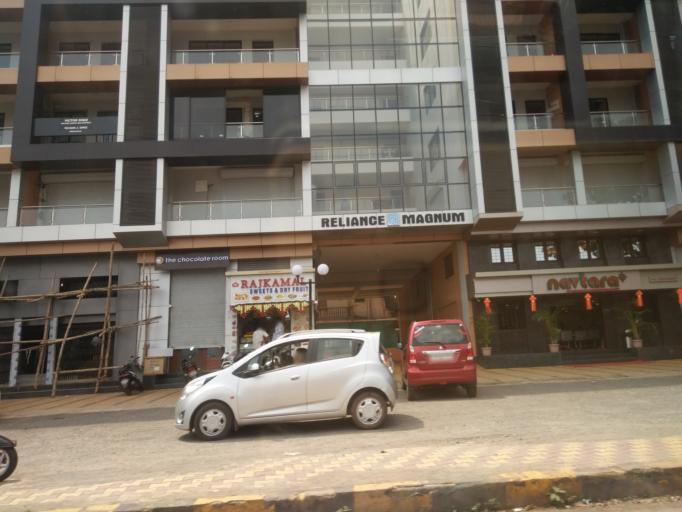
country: IN
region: Goa
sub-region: South Goa
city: Madgaon
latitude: 15.2875
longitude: 73.9552
